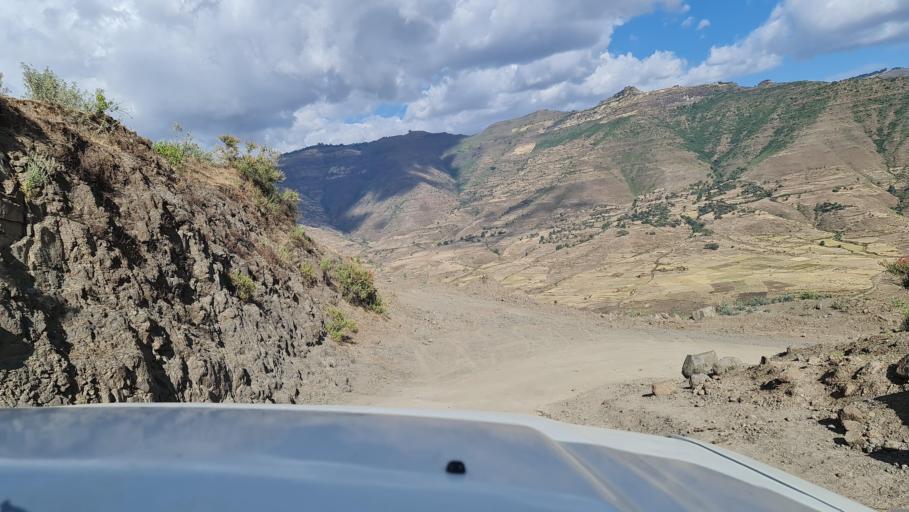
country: ET
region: Amhara
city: Debark'
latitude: 13.1197
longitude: 38.0217
